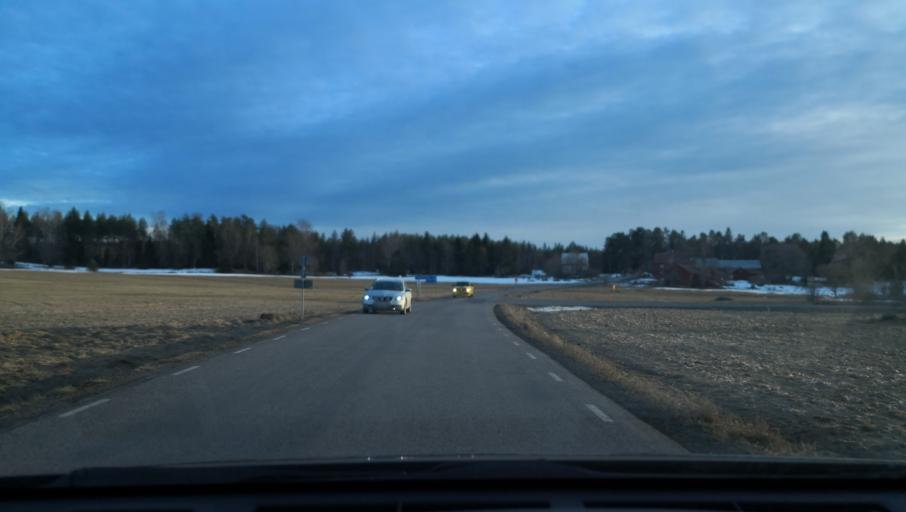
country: SE
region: Uppsala
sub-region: Osthammars Kommun
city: Osterbybruk
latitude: 60.2385
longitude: 17.9236
